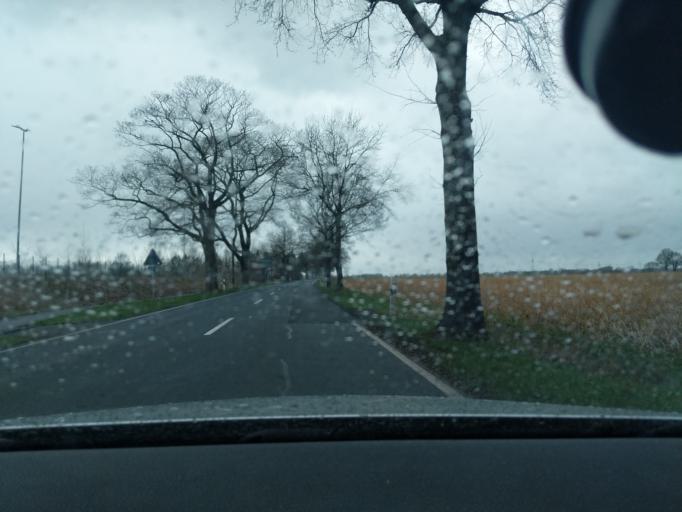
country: DE
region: Lower Saxony
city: Bargstedt
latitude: 53.4616
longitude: 9.4441
